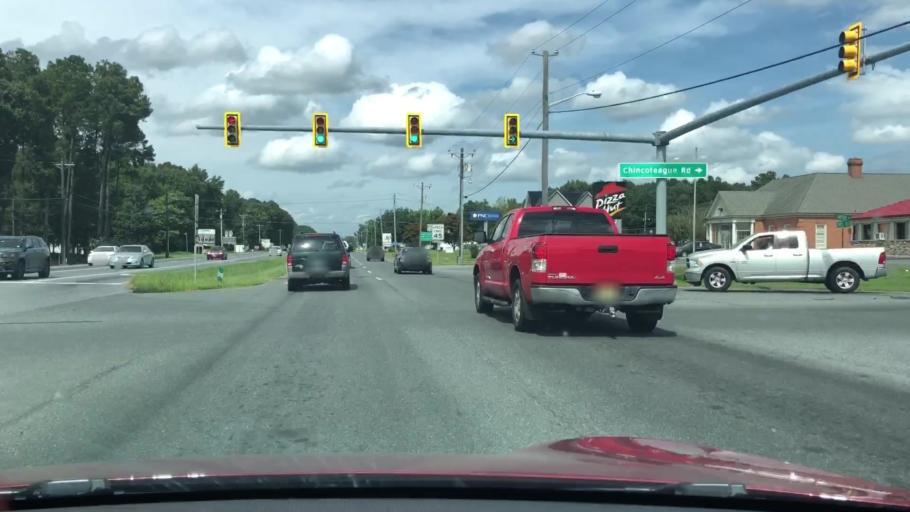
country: US
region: Virginia
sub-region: Accomack County
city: Wattsville
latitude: 37.9458
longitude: -75.5402
